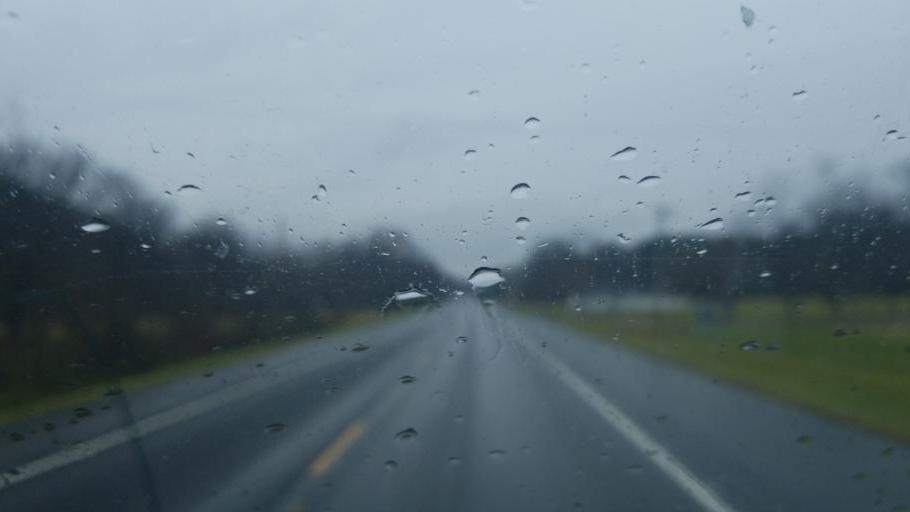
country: US
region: Indiana
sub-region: Brown County
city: Nashville
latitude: 39.1905
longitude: -86.1829
